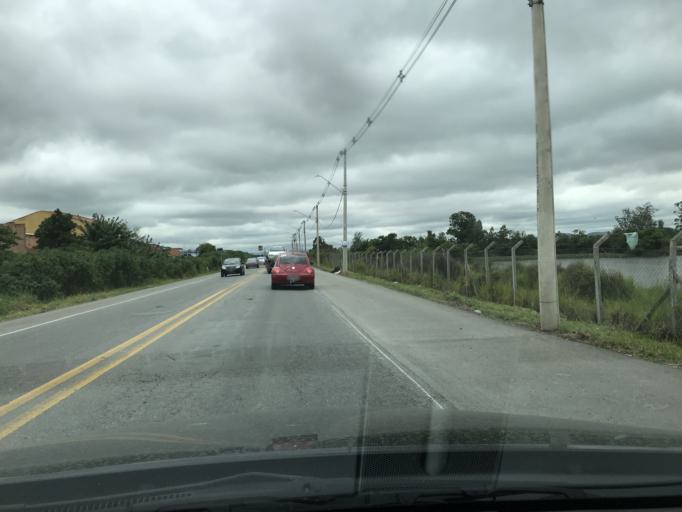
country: BR
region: Sao Paulo
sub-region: Itaquaquecetuba
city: Itaquaquecetuba
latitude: -23.4917
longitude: -46.3266
